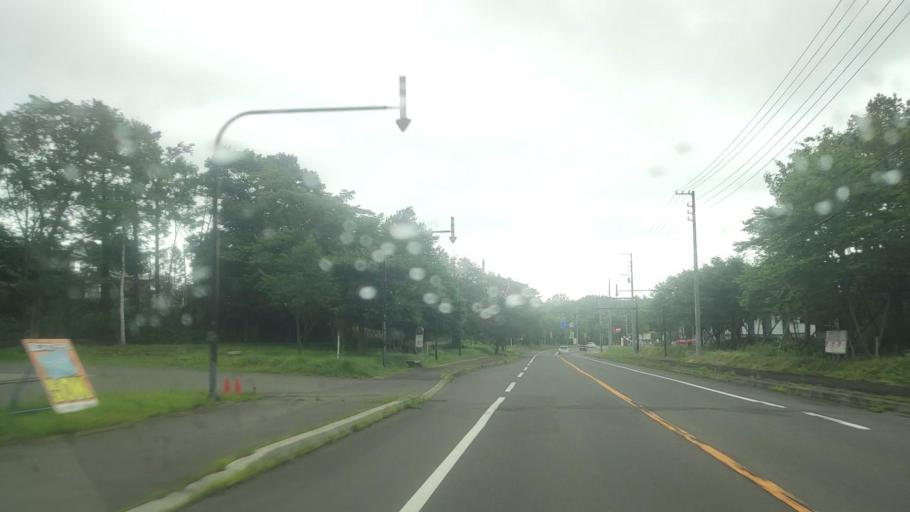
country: JP
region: Hokkaido
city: Shiraoi
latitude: 42.4758
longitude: 141.1473
